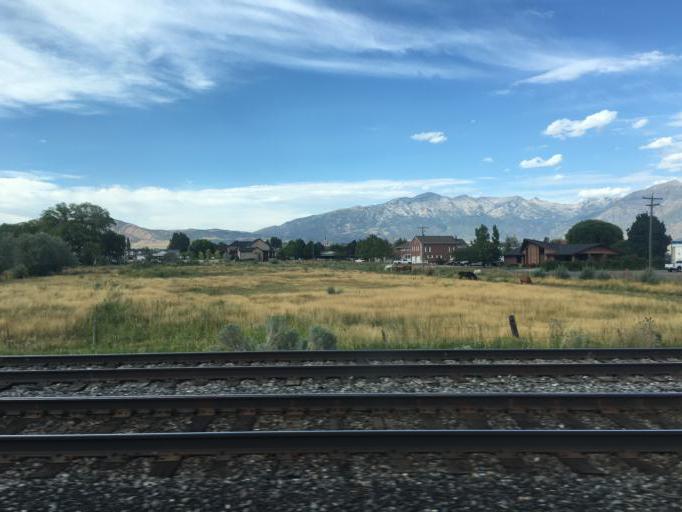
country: US
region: Utah
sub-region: Utah County
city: Lehi
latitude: 40.3790
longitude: -111.8405
